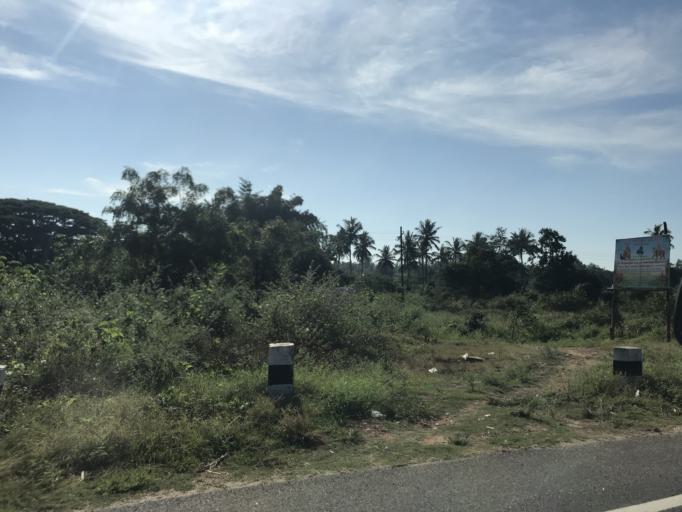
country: IN
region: Karnataka
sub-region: Mysore
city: Mysore
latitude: 12.1944
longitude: 76.5440
